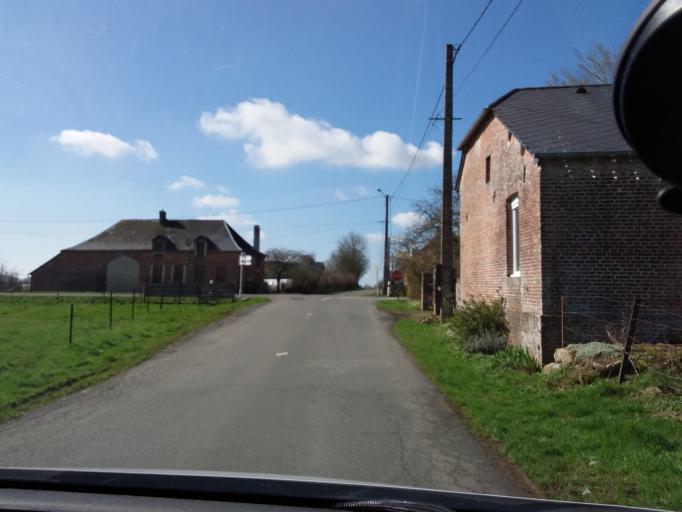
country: FR
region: Picardie
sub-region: Departement de l'Aisne
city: Origny-en-Thierache
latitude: 49.8381
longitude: 4.0620
